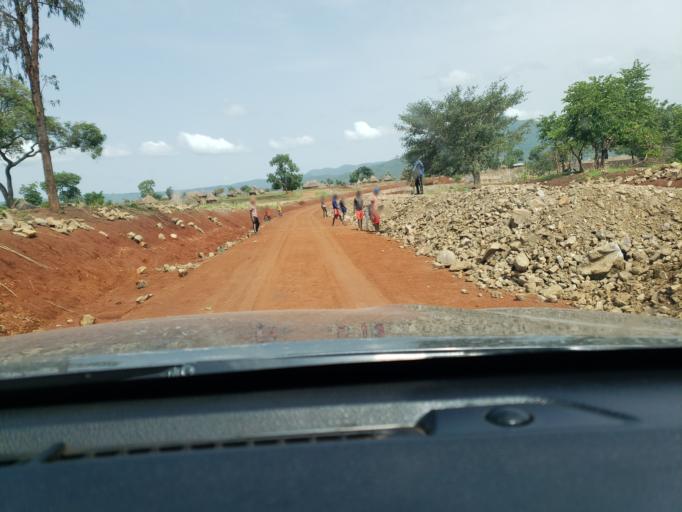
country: ET
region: Oromiya
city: Mendi
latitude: 10.1178
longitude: 35.1437
